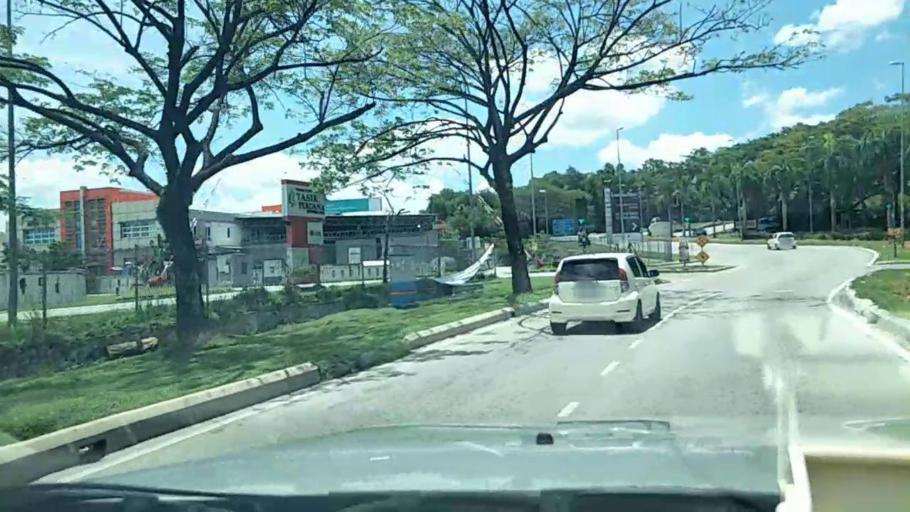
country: MY
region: Putrajaya
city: Putrajaya
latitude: 2.9613
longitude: 101.6175
